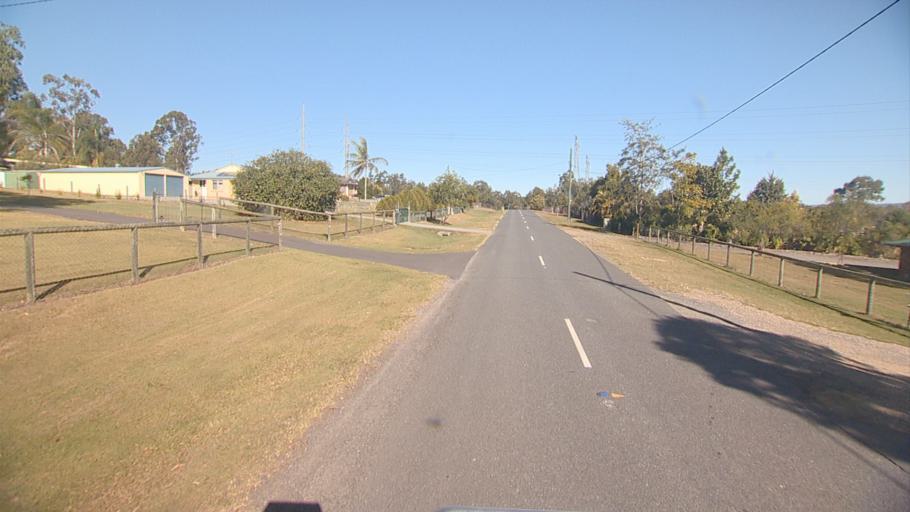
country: AU
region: Queensland
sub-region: Logan
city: North Maclean
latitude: -27.7316
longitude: 152.9612
